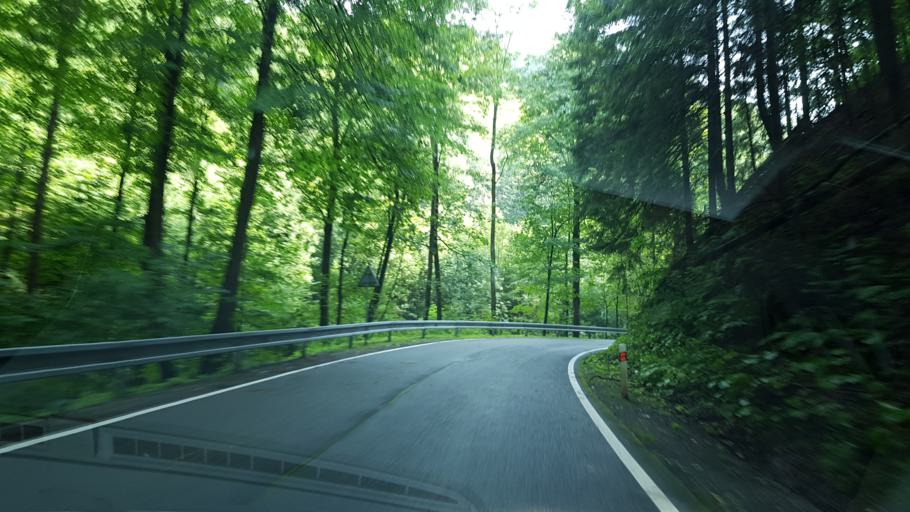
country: CZ
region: Olomoucky
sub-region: Okres Jesenik
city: Jesenik
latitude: 50.2080
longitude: 17.2458
